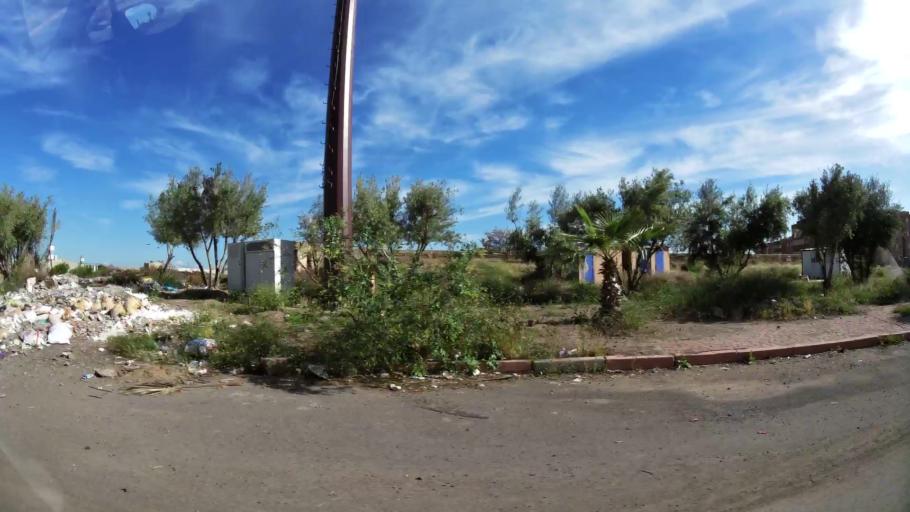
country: MA
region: Marrakech-Tensift-Al Haouz
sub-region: Marrakech
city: Marrakesh
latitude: 31.6735
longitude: -8.0518
